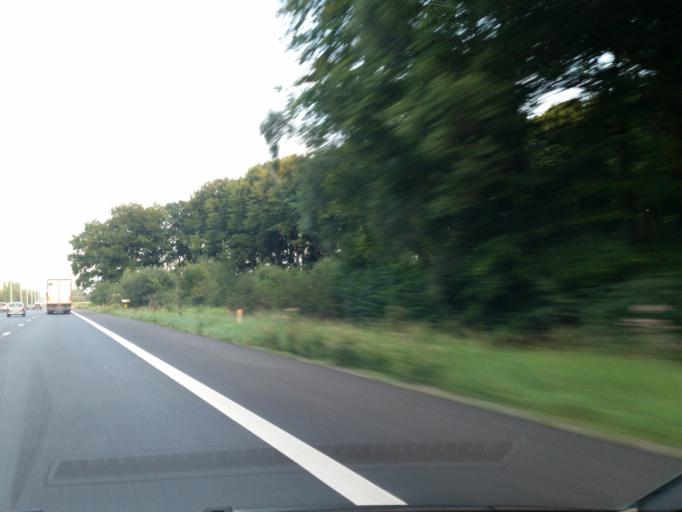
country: BE
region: Flanders
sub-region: Provincie Oost-Vlaanderen
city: Knesselare
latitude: 51.0989
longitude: 3.3894
